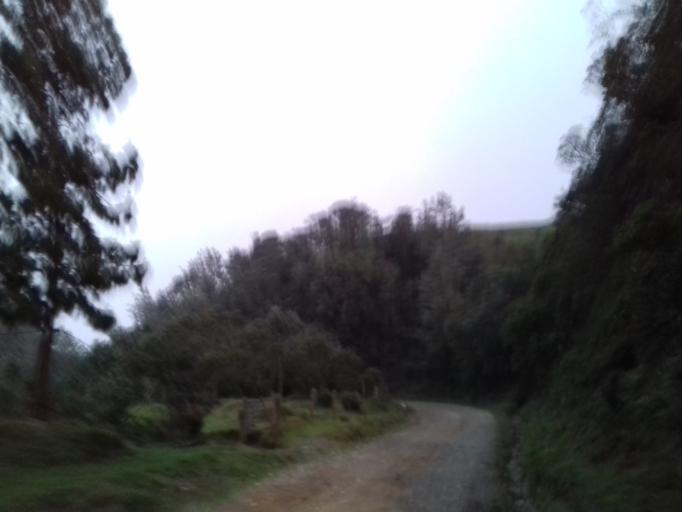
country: CO
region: Quindio
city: Salento
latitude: 4.5655
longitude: -75.5179
